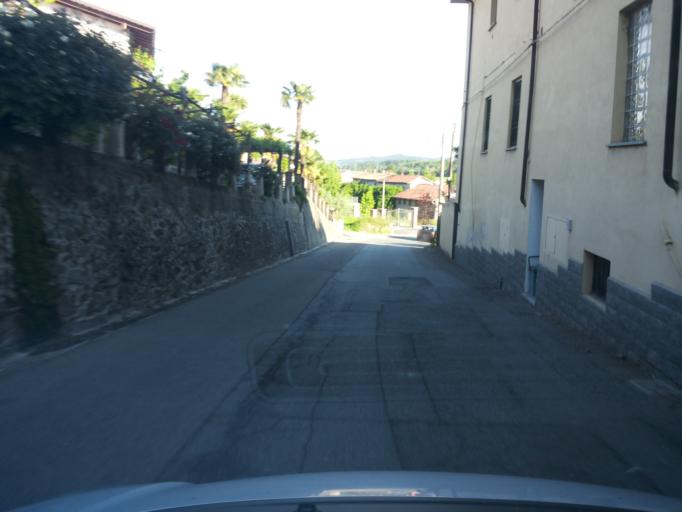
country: IT
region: Piedmont
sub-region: Provincia di Torino
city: Piverone
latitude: 45.4426
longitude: 8.0115
